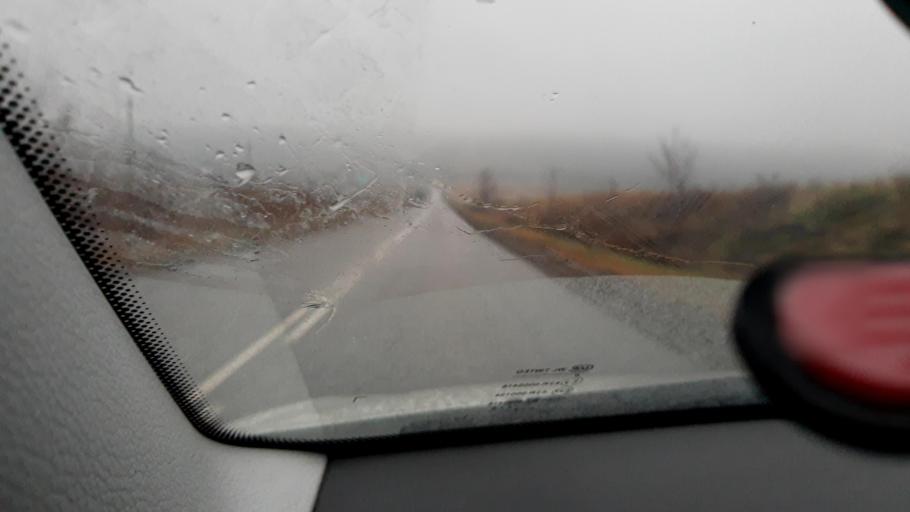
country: RU
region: Bashkortostan
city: Iglino
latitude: 54.9005
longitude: 56.1913
